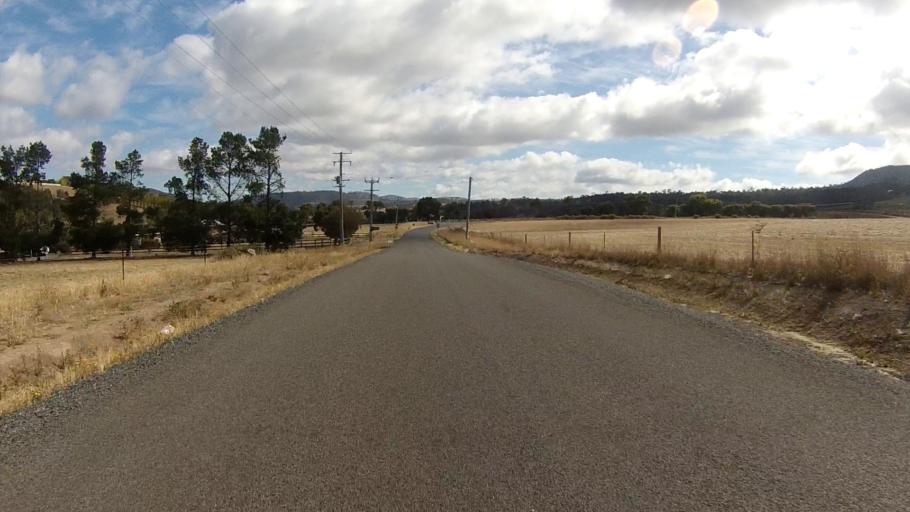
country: AU
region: Tasmania
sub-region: Brighton
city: Old Beach
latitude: -42.7614
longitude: 147.3007
